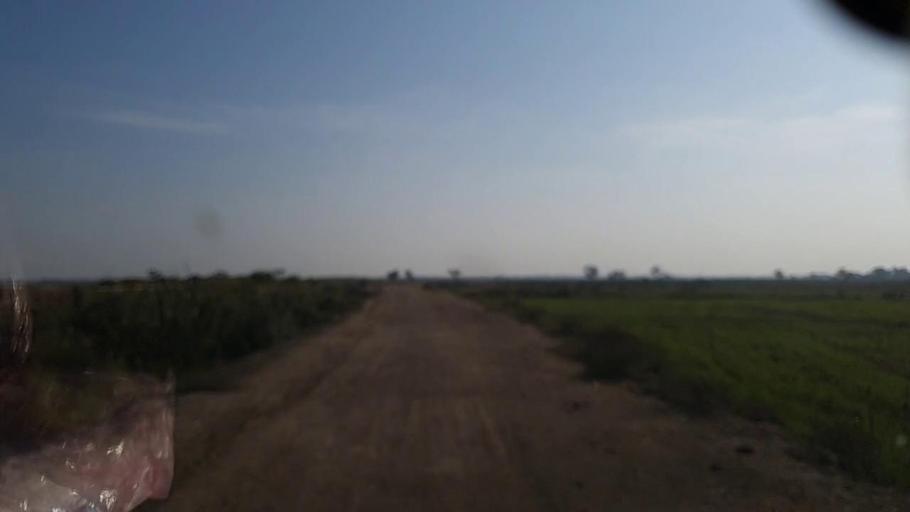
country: PK
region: Sindh
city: Jacobabad
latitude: 28.2958
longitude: 68.5581
